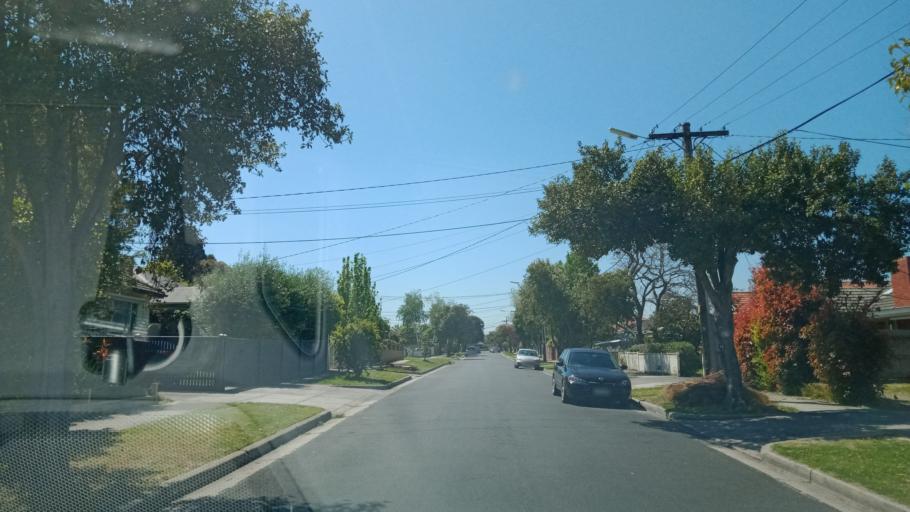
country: AU
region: Victoria
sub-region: Monash
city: Oakleigh South
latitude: -37.9218
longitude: 145.0757
